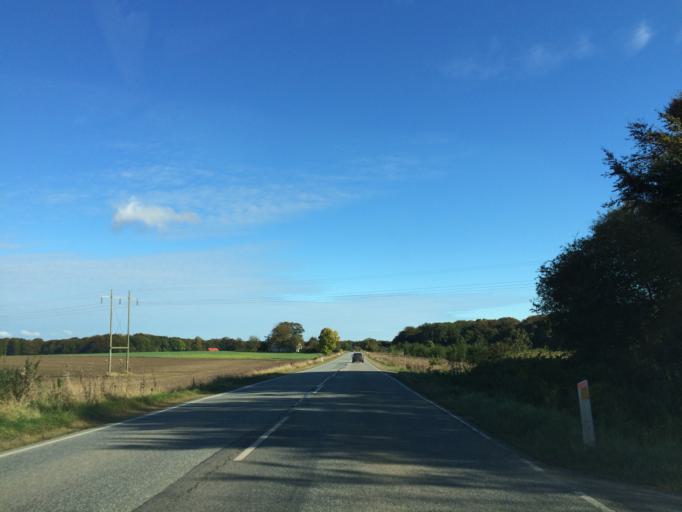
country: DK
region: Central Jutland
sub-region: Randers Kommune
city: Langa
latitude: 56.3887
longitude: 9.9665
